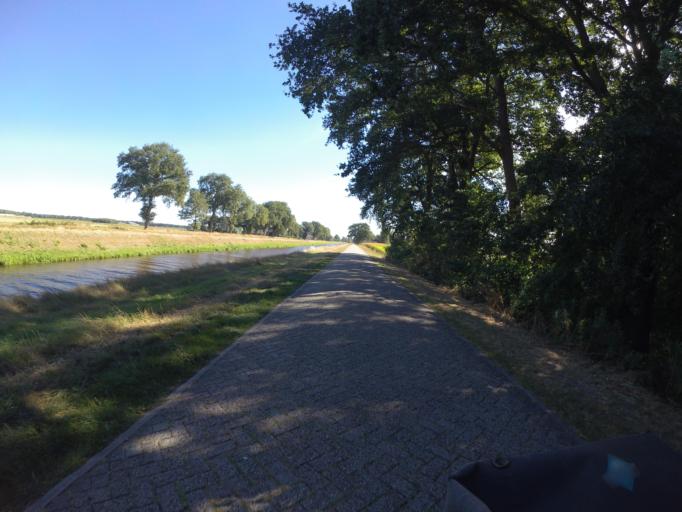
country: NL
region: Drenthe
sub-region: Gemeente Hoogeveen
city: Hoogeveen
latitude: 52.7269
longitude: 6.6162
